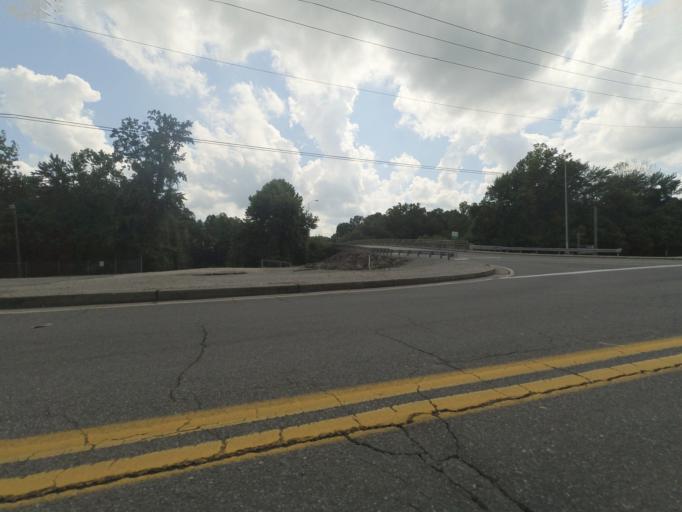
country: US
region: West Virginia
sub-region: Cabell County
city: Huntington
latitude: 38.4131
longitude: -82.3859
